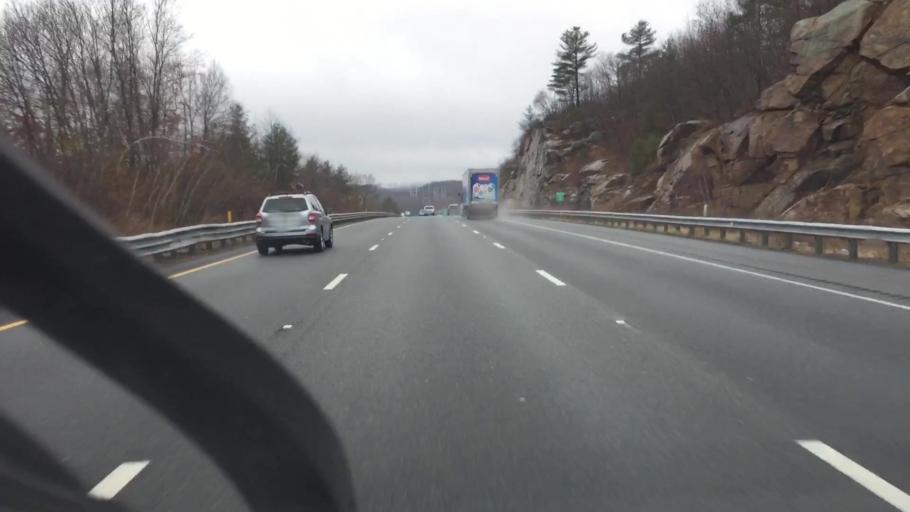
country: US
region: Massachusetts
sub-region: Worcester County
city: Milford
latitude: 42.1632
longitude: -71.5000
